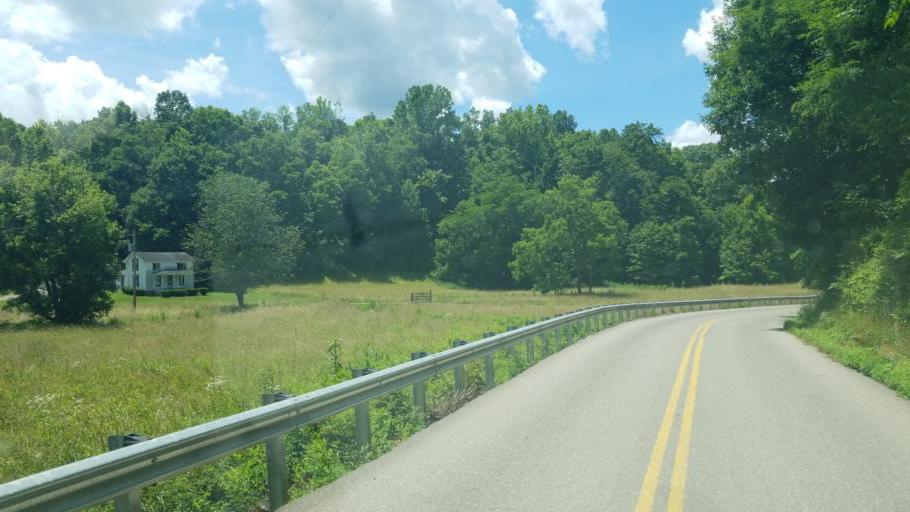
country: US
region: Ohio
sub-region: Gallia County
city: Gallipolis
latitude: 38.7242
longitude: -82.3604
